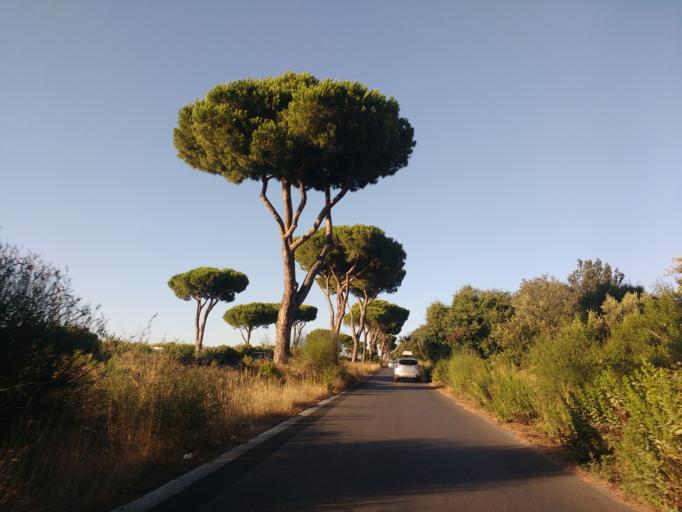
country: IT
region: Latium
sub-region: Citta metropolitana di Roma Capitale
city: Vitinia
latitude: 41.7618
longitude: 12.3791
